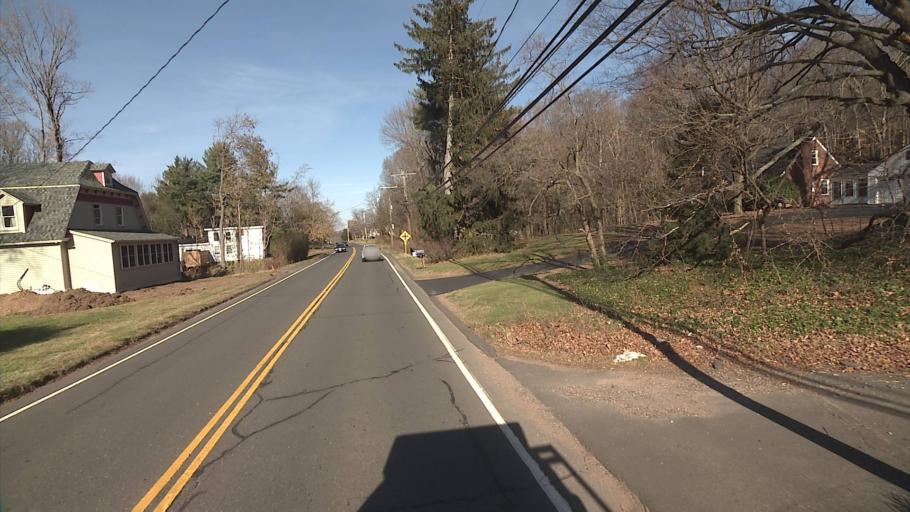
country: US
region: Connecticut
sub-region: Hartford County
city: Glastonbury Center
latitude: 41.6552
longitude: -72.6041
